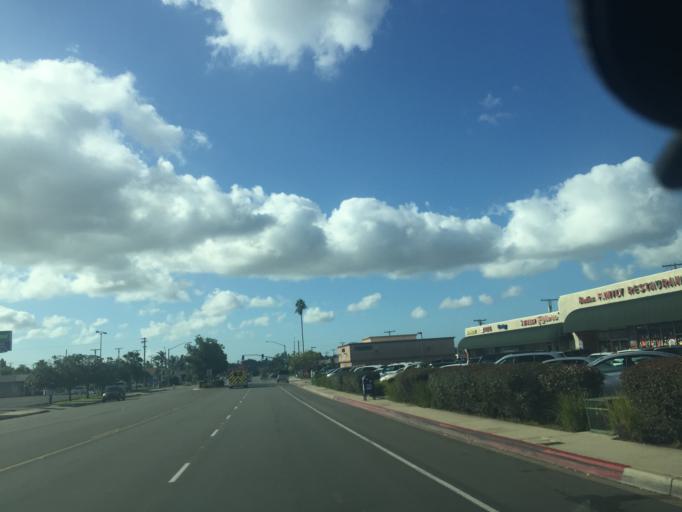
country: US
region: California
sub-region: San Diego County
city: La Mesa
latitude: 32.7919
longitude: -117.0816
